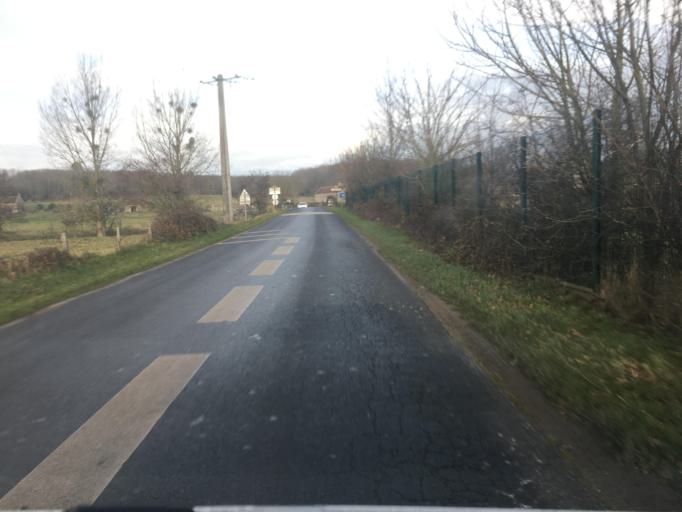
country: FR
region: Lower Normandy
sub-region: Departement du Calvados
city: Creully
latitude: 49.2872
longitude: -0.5406
